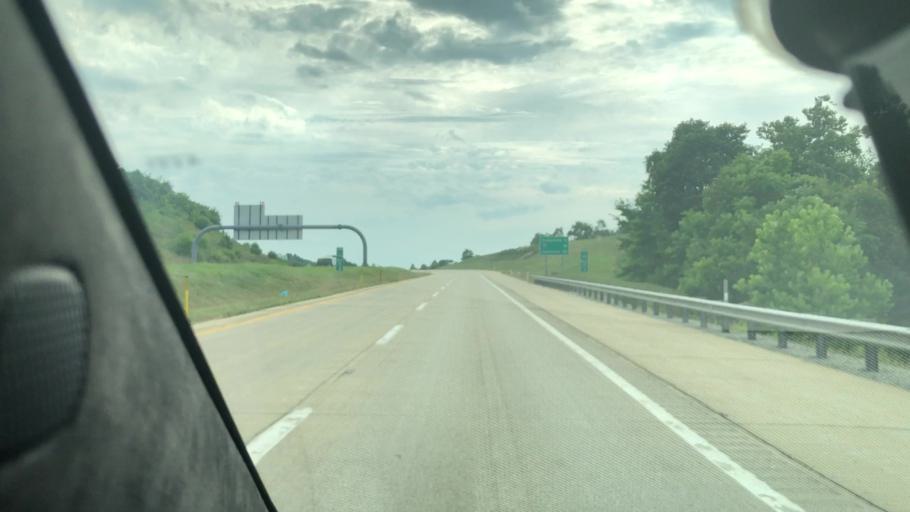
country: US
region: Pennsylvania
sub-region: Allegheny County
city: Jefferson Hills
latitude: 40.2785
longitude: -79.9435
